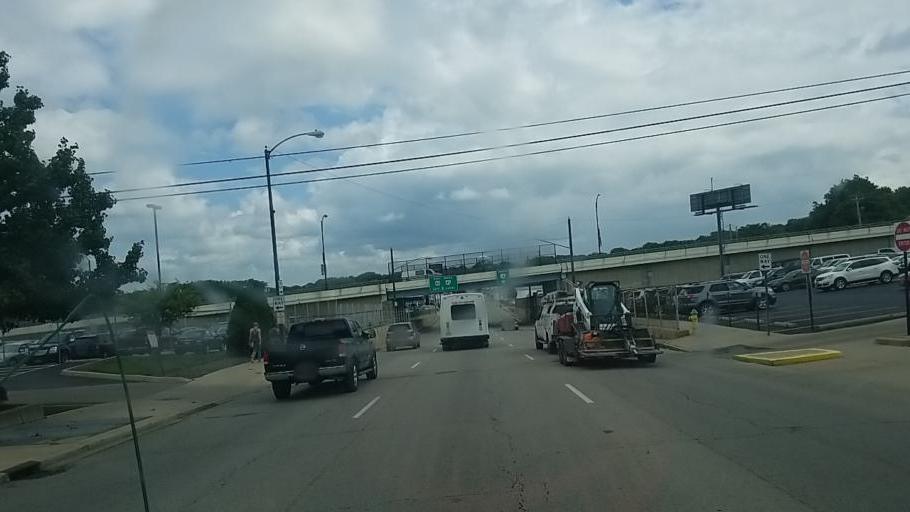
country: US
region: Ohio
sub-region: Clark County
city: Springfield
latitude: 39.9257
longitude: -83.8077
